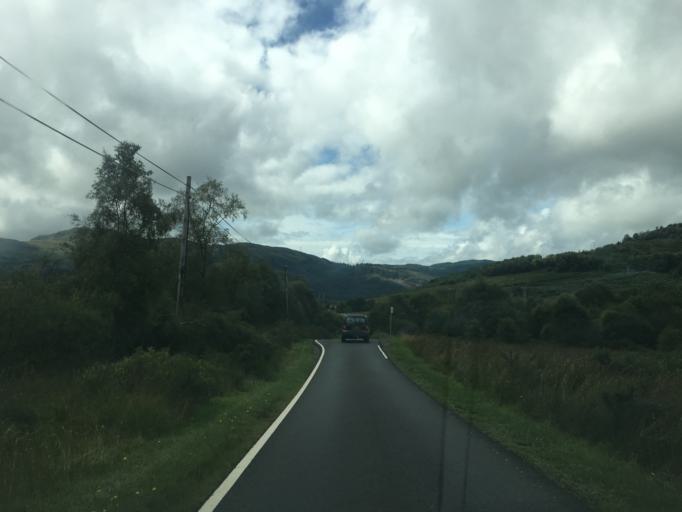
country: GB
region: Scotland
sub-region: Argyll and Bute
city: Port Bannatyne
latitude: 55.9880
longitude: -5.1631
